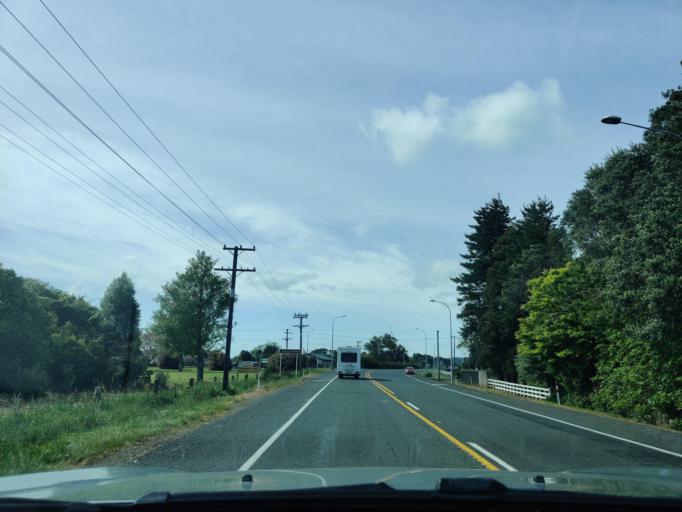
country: NZ
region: Taranaki
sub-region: New Plymouth District
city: New Plymouth
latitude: -39.0922
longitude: 174.1045
